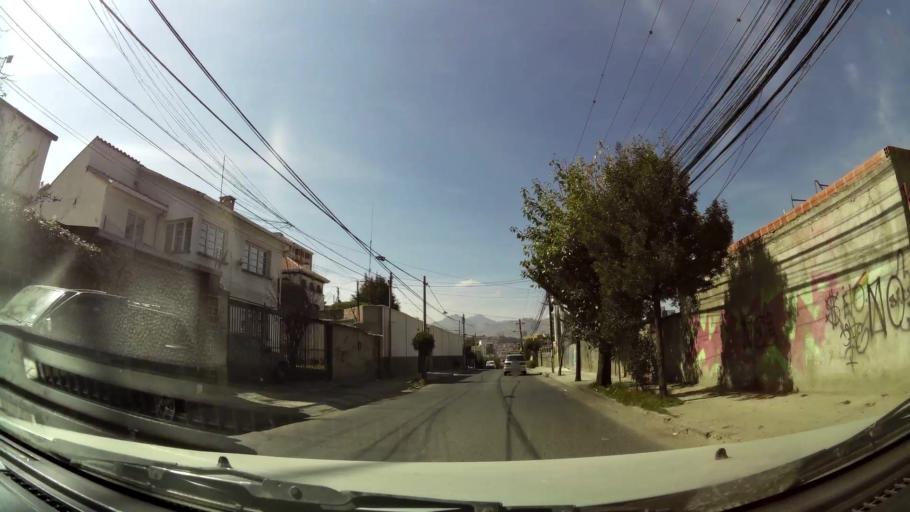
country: BO
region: La Paz
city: La Paz
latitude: -16.5240
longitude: -68.1107
